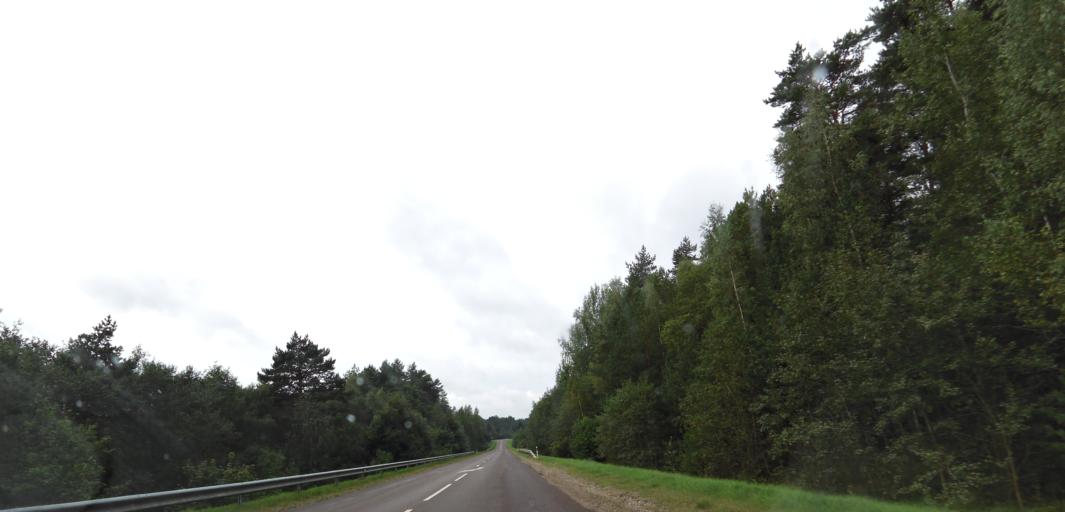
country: LT
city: Moletai
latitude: 55.2157
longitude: 25.3735
